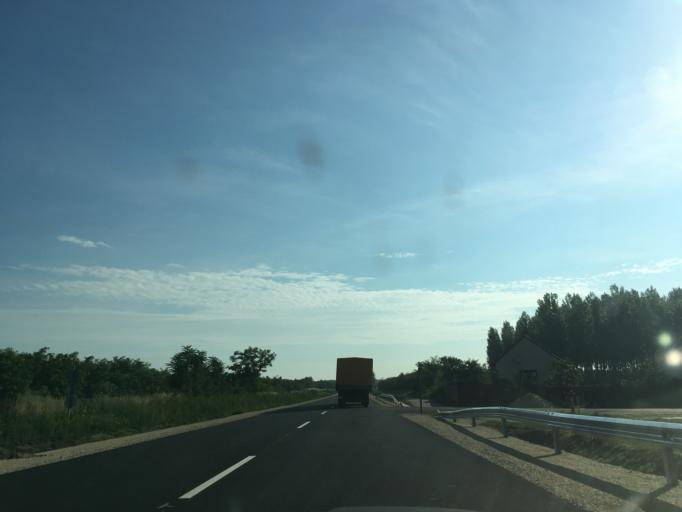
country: HU
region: Hajdu-Bihar
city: Hajdusamson
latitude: 47.6385
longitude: 21.8067
